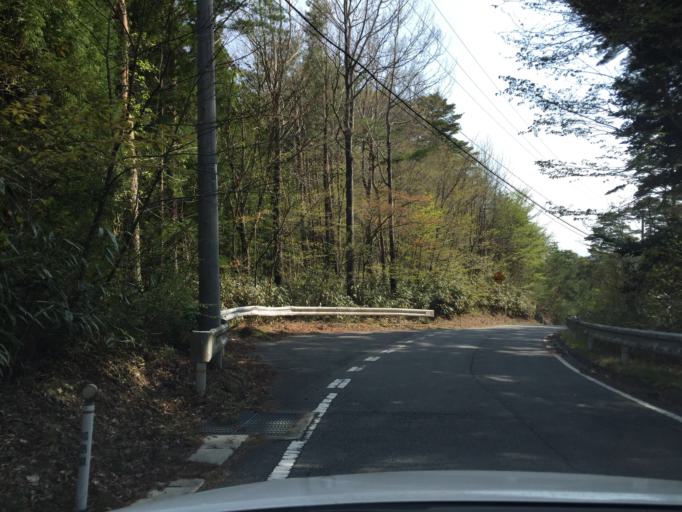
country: JP
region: Fukushima
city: Iwaki
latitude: 37.1944
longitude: 140.8527
